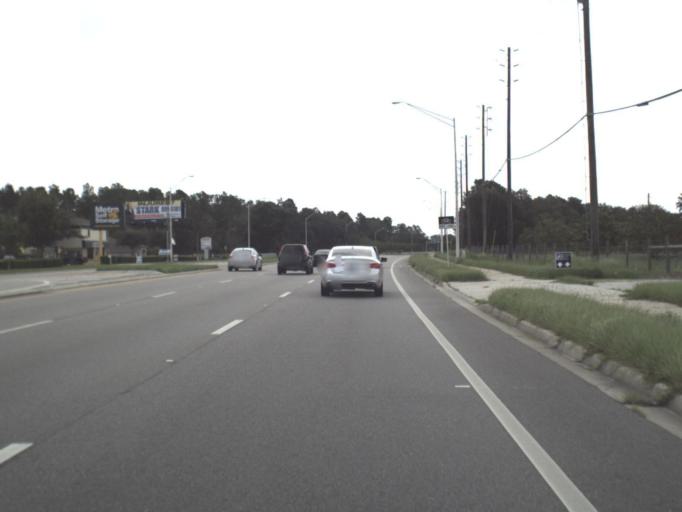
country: US
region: Florida
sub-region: Pasco County
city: Wesley Chapel
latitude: 28.2392
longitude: -82.3389
